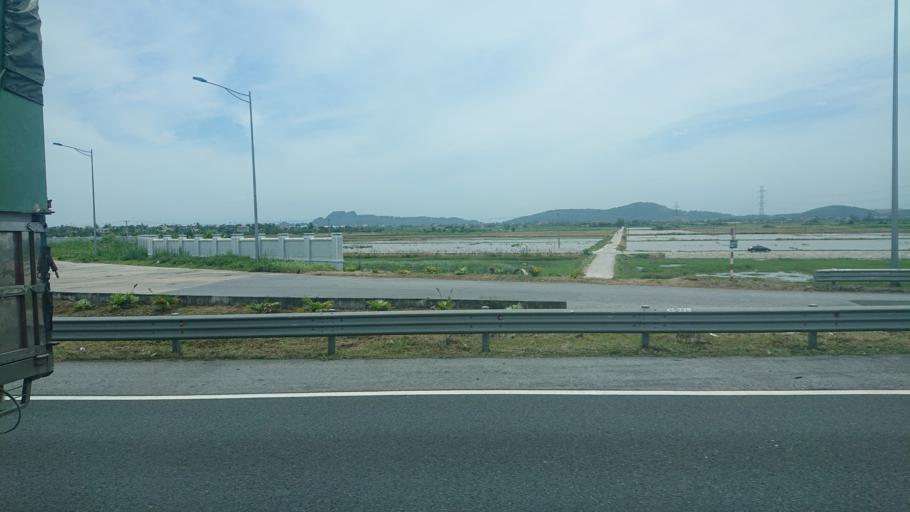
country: VN
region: Hai Phong
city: An Lao
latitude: 20.7925
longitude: 106.5497
